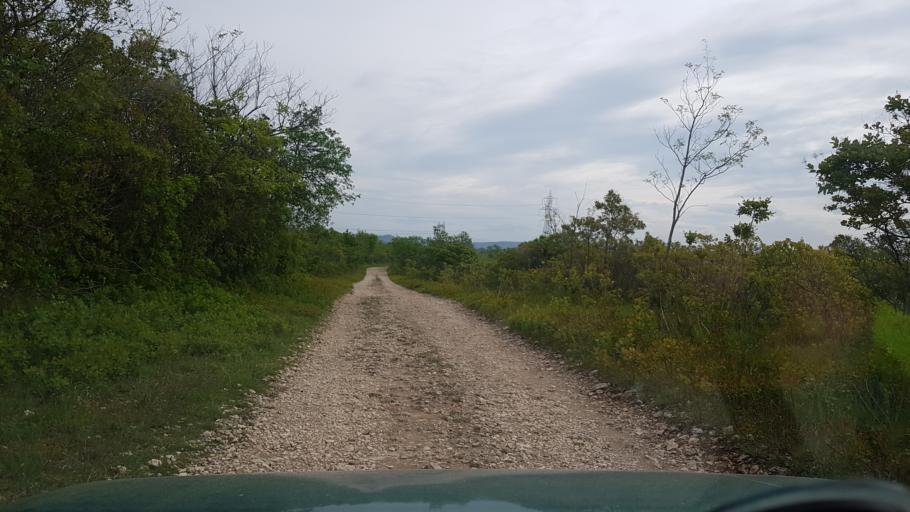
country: IT
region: Friuli Venezia Giulia
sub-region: Provincia di Gorizia
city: Doberdo del Lago
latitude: 45.8455
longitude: 13.5193
